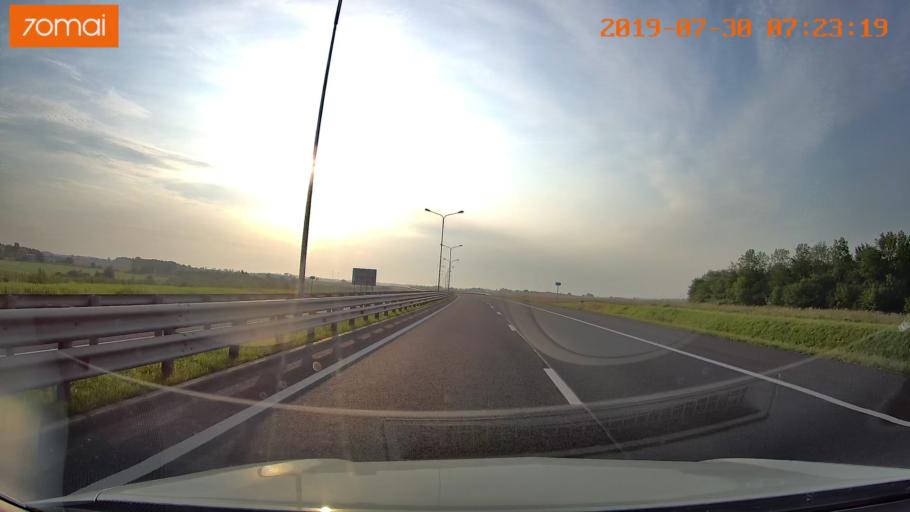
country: RU
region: Kaliningrad
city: Bol'shoe Isakovo
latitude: 54.6918
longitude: 20.7803
